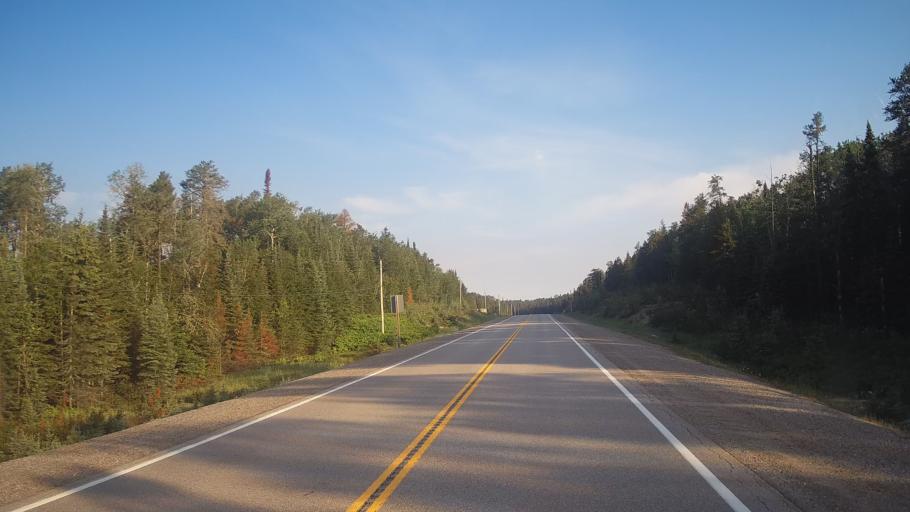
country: CA
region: Ontario
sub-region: Rainy River District
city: Atikokan
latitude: 49.3956
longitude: -91.6075
